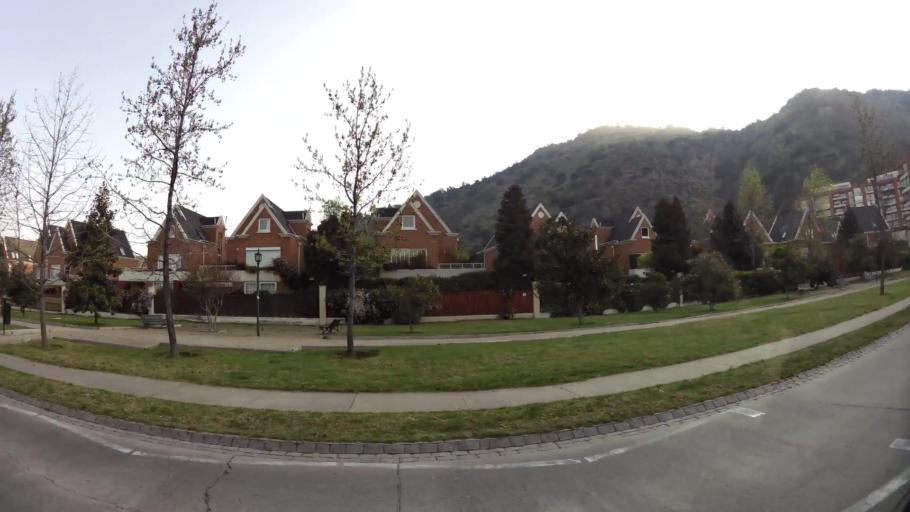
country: CL
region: Santiago Metropolitan
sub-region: Provincia de Santiago
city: Villa Presidente Frei, Nunoa, Santiago, Chile
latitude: -33.3550
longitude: -70.5451
